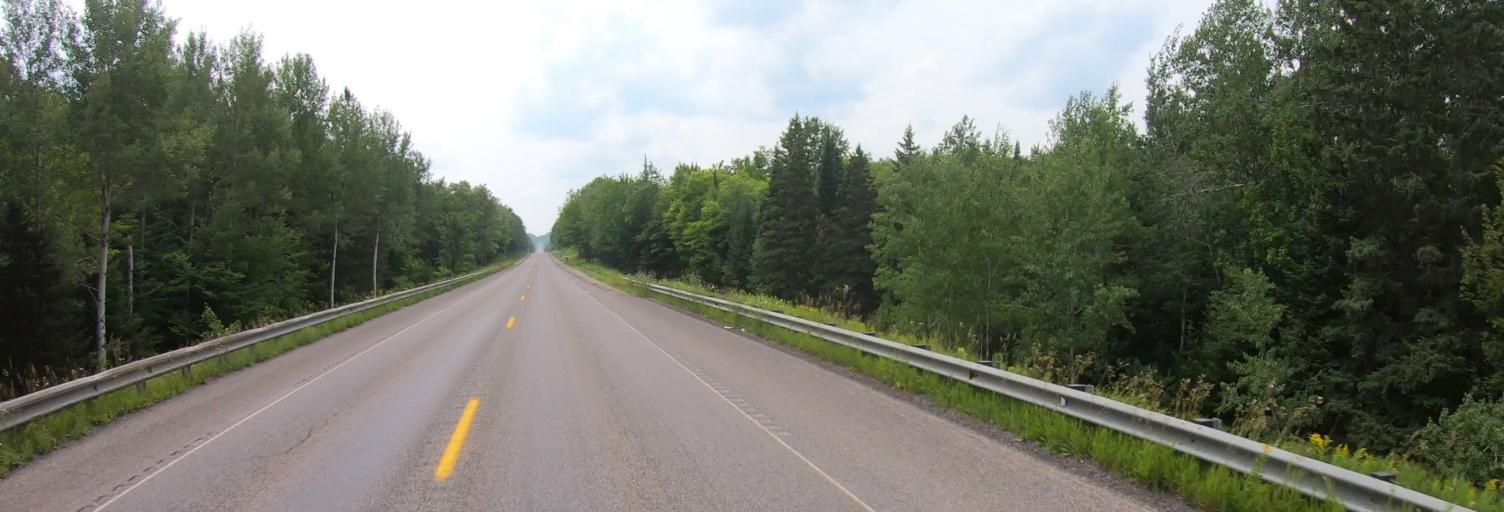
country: US
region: Michigan
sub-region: Alger County
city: Munising
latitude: 46.3716
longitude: -86.7053
